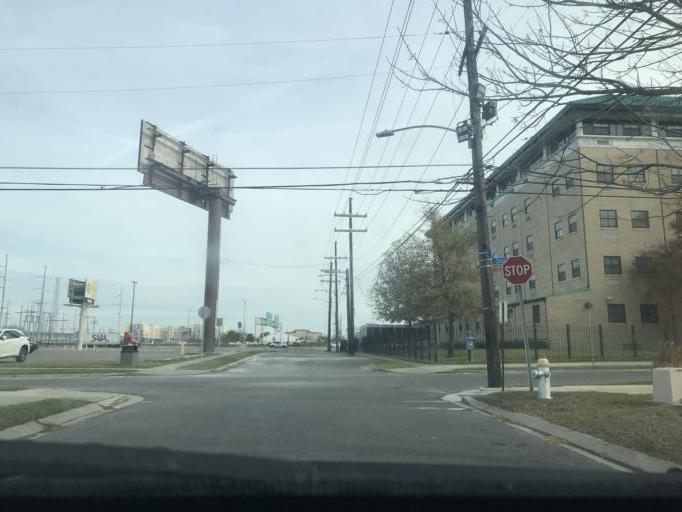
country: US
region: Louisiana
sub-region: Orleans Parish
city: New Orleans
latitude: 29.9621
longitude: -90.1027
